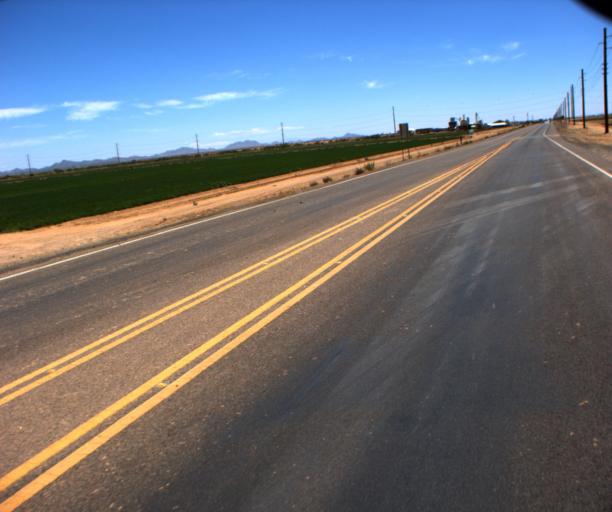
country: US
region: Arizona
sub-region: Pinal County
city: Casa Grande
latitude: 32.8793
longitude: -111.9569
